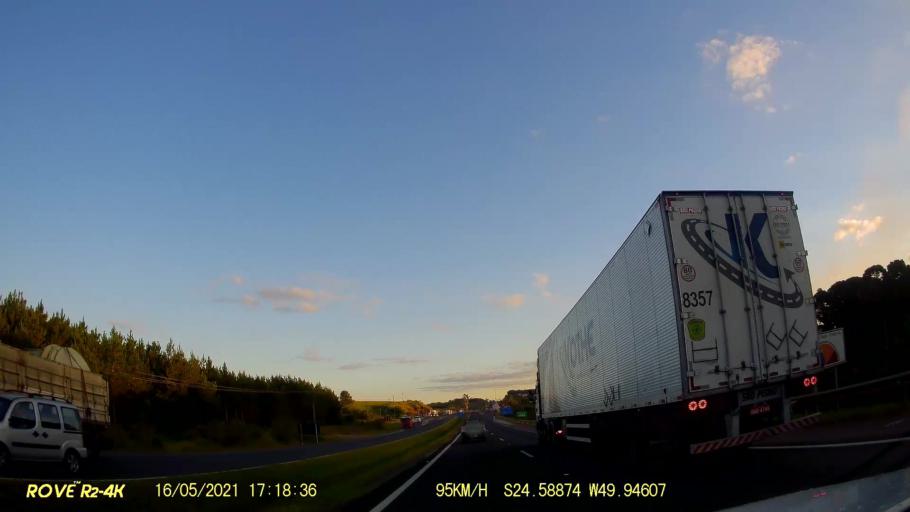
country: BR
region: Parana
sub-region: Pirai Do Sul
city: Pirai do Sul
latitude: -24.5889
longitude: -49.9462
